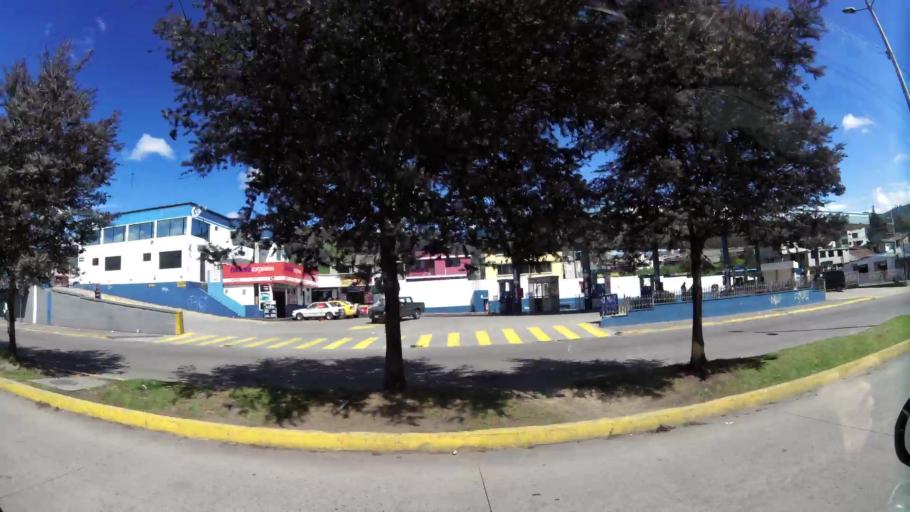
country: EC
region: Pichincha
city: Quito
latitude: -0.2971
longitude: -78.5587
